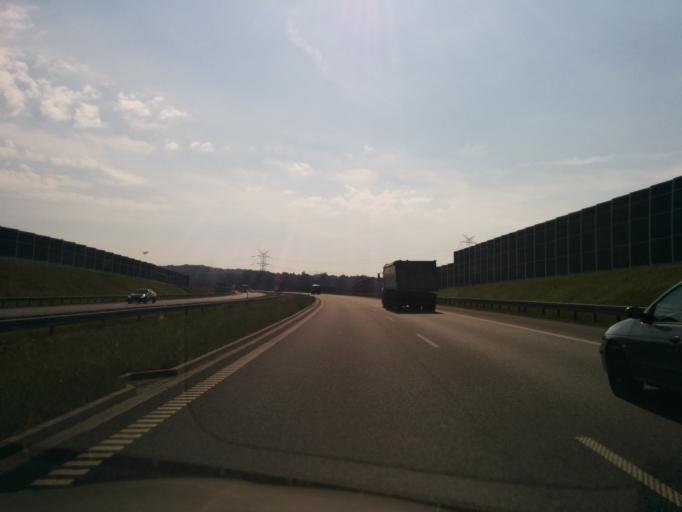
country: PL
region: Silesian Voivodeship
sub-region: Powiat tarnogorski
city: Wieszowa
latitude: 50.3848
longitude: 18.8194
